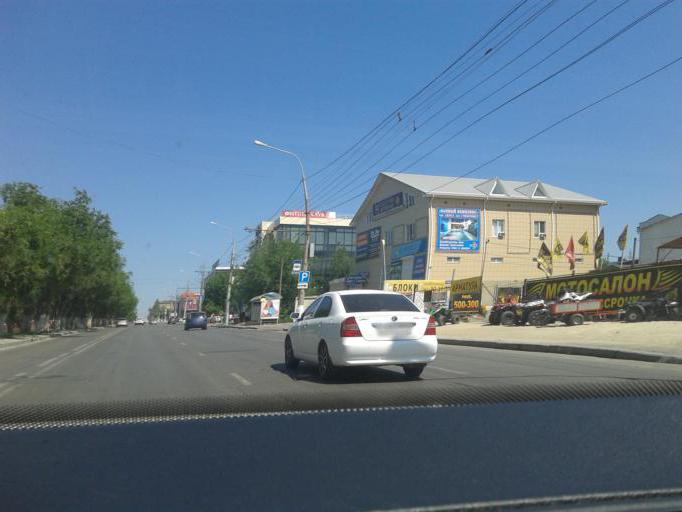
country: RU
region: Volgograd
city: Volgograd
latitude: 48.7266
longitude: 44.5003
